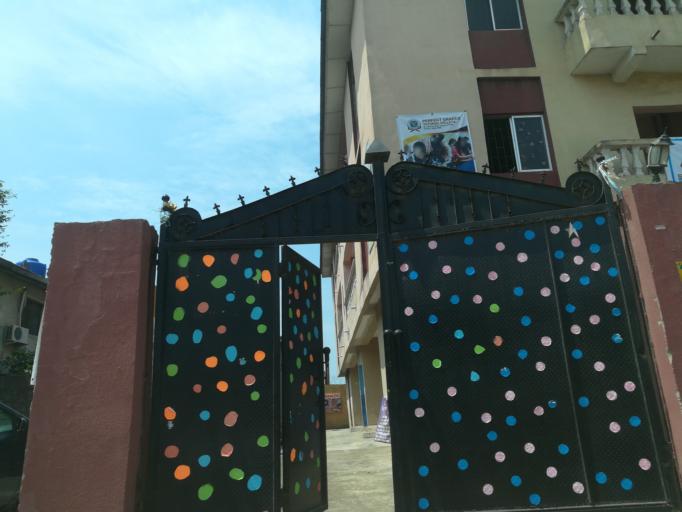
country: NG
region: Lagos
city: Ikorodu
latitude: 6.6214
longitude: 3.4976
